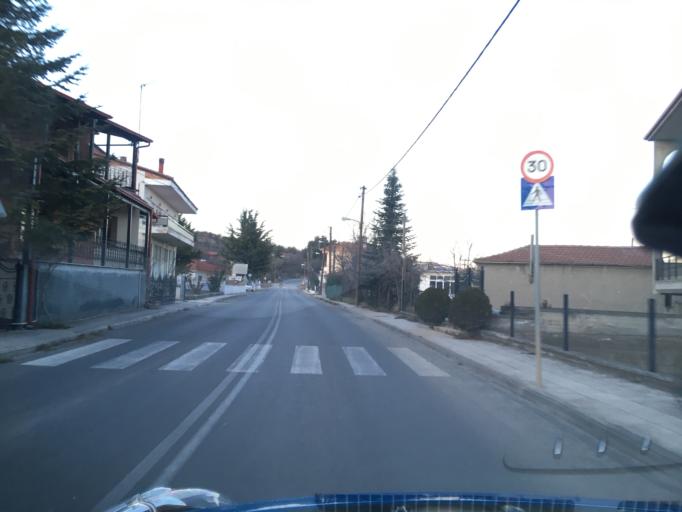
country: GR
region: West Macedonia
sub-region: Nomos Kozanis
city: Kozani
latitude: 40.2719
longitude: 21.7815
